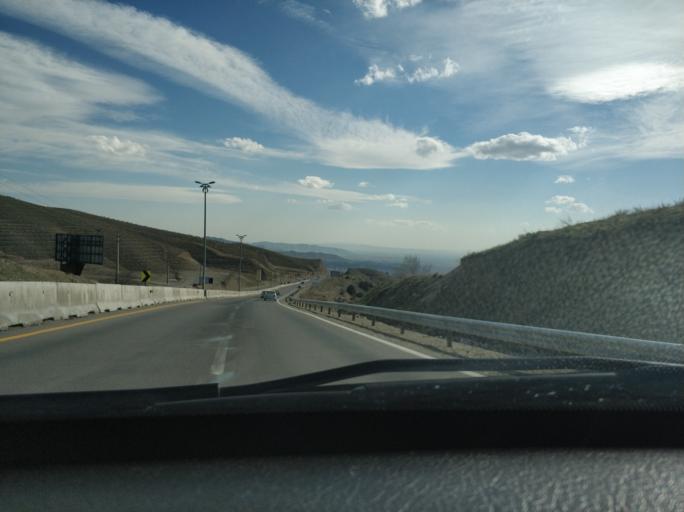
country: IR
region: Tehran
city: Tajrish
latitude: 35.7966
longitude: 51.5713
